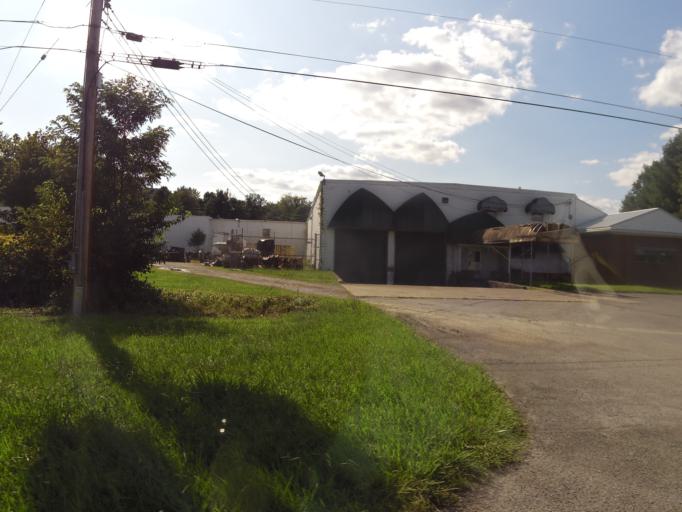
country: US
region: Kentucky
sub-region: Bell County
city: Middlesboro
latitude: 36.6012
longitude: -83.7294
